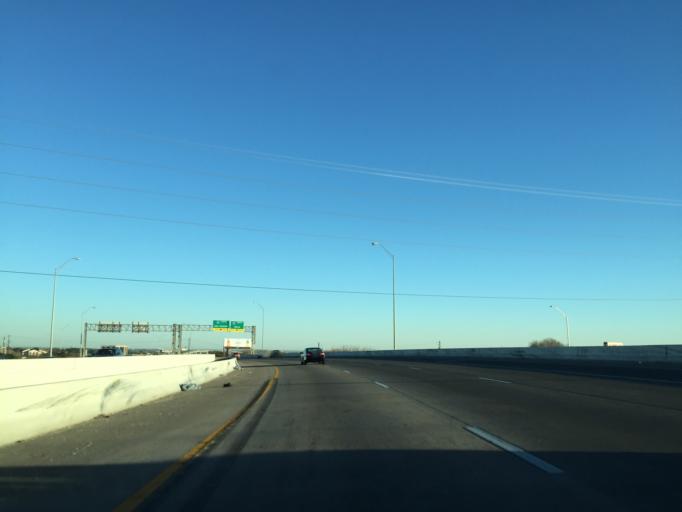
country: US
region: Texas
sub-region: Travis County
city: Austin
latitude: 30.3478
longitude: -97.7127
